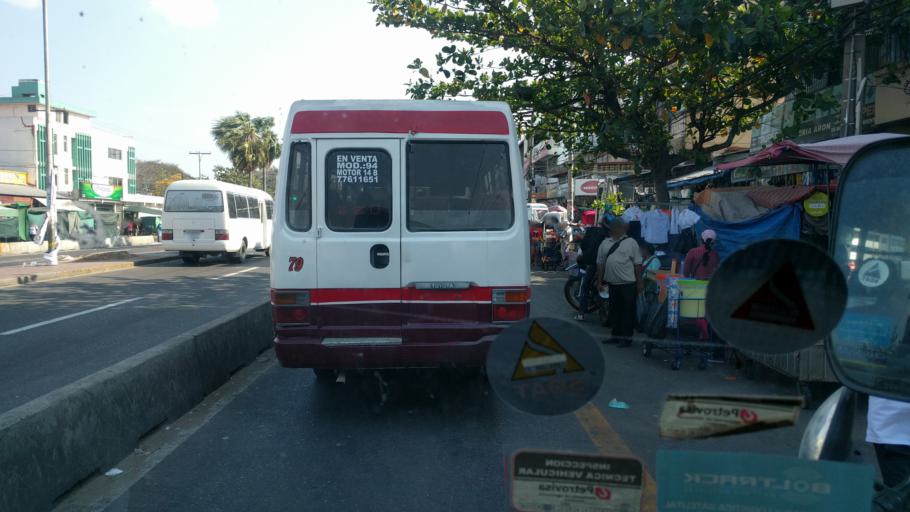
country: BO
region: Santa Cruz
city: Santa Cruz de la Sierra
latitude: -17.7968
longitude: -63.1915
